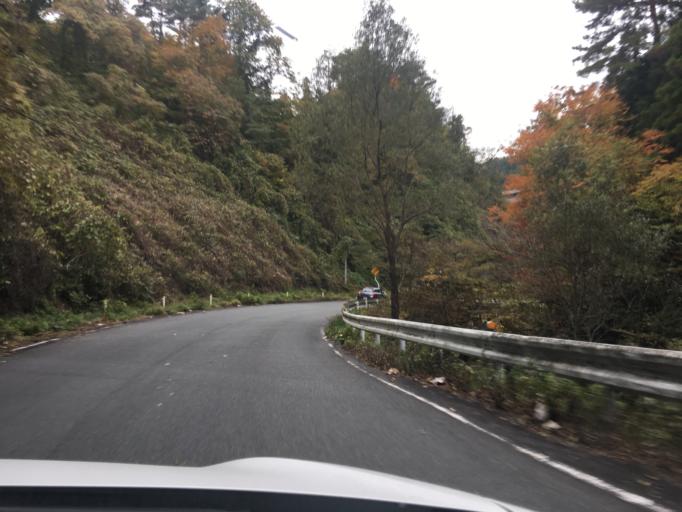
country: JP
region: Fukushima
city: Iwaki
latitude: 37.1601
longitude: 140.7336
